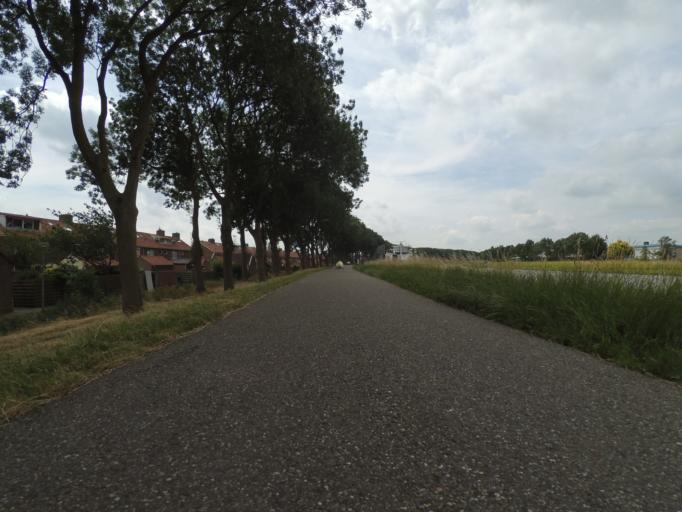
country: NL
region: South Holland
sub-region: Gemeente Gorinchem
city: Gorinchem
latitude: 51.8666
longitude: 4.9960
